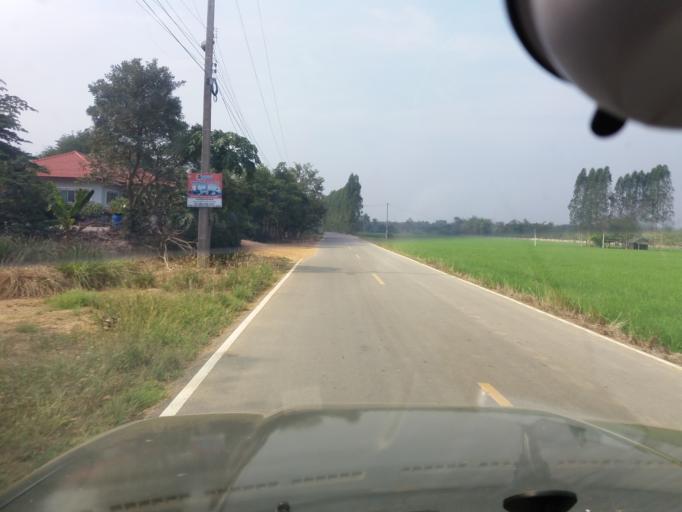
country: TH
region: Suphan Buri
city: Doem Bang Nang Buat
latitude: 14.8929
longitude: 100.1802
